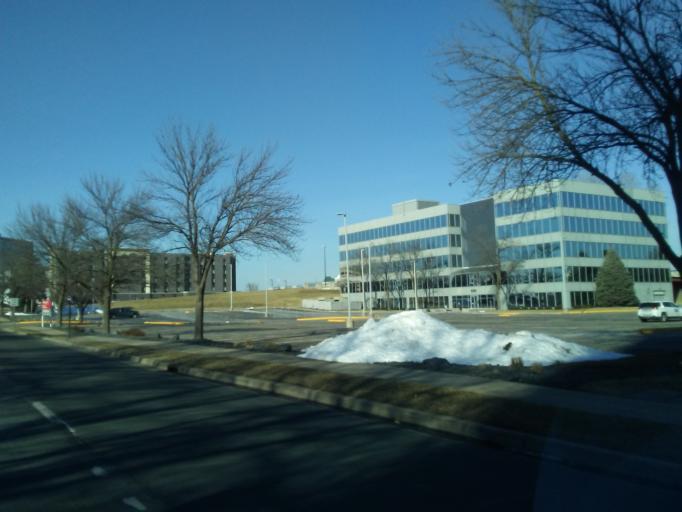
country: US
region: Minnesota
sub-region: Hennepin County
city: Edina
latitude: 44.8533
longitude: -93.3522
